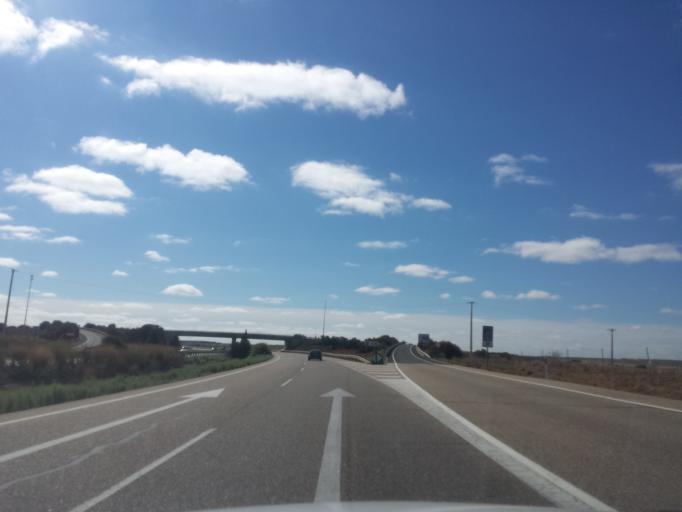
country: ES
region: Castille and Leon
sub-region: Provincia de Zamora
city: Villalpando
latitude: 41.8586
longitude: -5.4253
